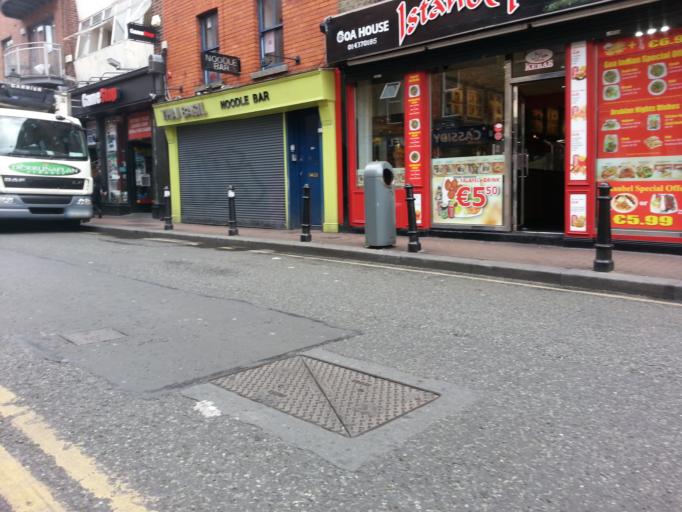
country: IE
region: Leinster
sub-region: Dublin City
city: Dublin
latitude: 53.3474
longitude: -6.2635
